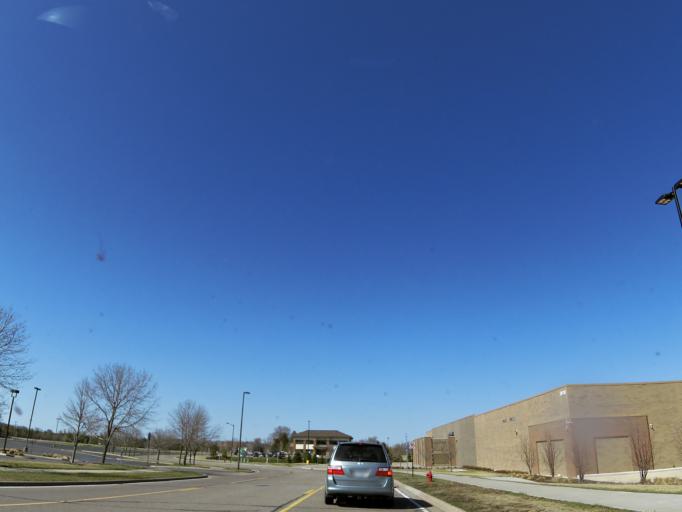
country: US
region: Minnesota
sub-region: Dakota County
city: Lakeville
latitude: 44.6496
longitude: -93.2982
